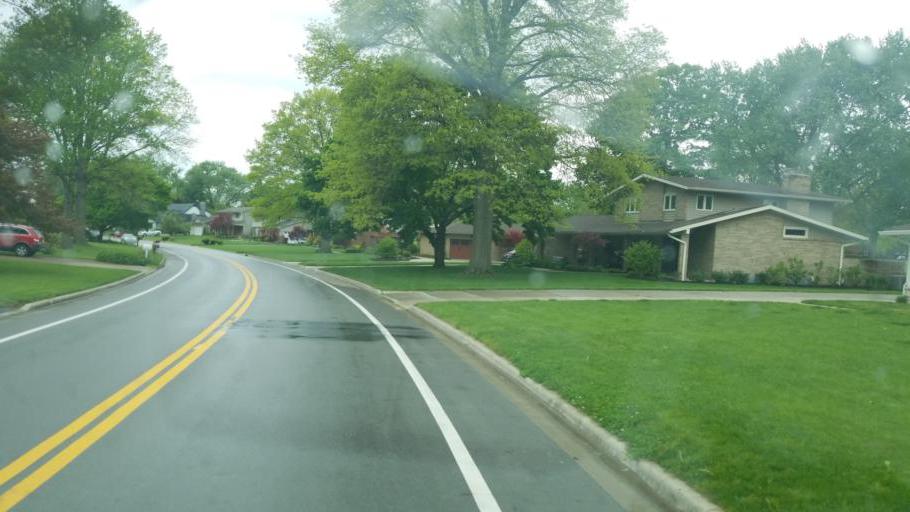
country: US
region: Ohio
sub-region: Delaware County
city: Powell
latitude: 40.1252
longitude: -83.0521
